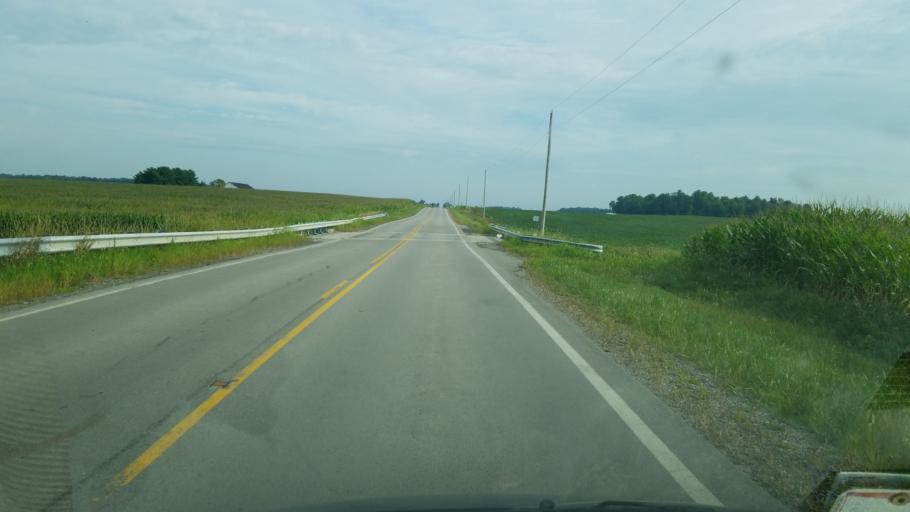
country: US
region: Ohio
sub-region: Crawford County
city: Bucyrus
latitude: 40.9262
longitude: -83.0166
